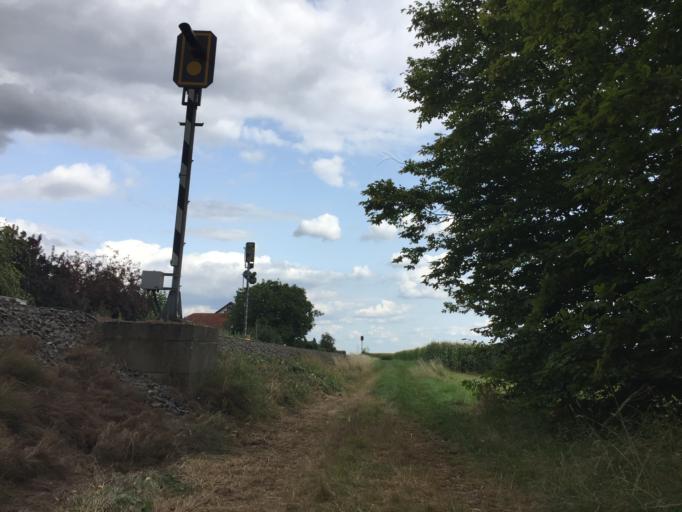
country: DE
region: Hesse
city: Liederbach
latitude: 50.1173
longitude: 8.4898
